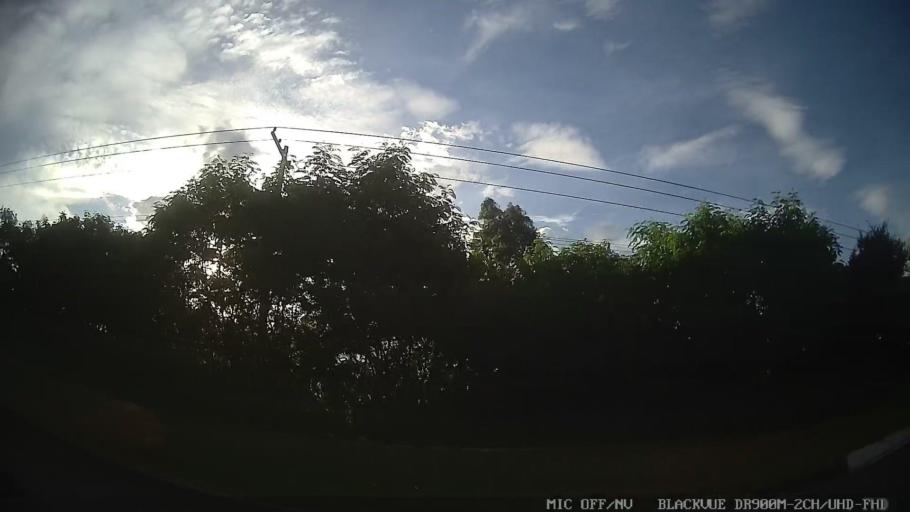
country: BR
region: Sao Paulo
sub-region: Tiete
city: Tiete
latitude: -23.0942
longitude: -47.7228
